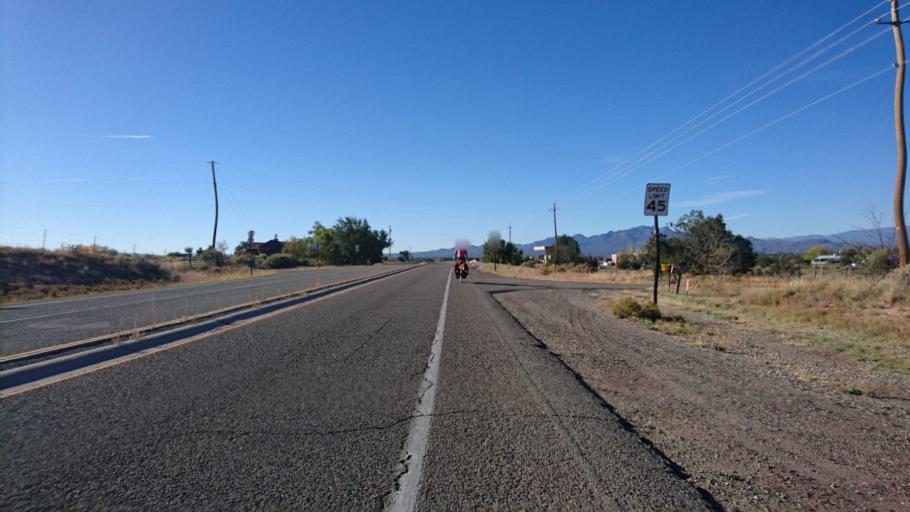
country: US
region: New Mexico
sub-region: Santa Fe County
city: La Cienega
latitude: 35.4931
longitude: -106.0657
